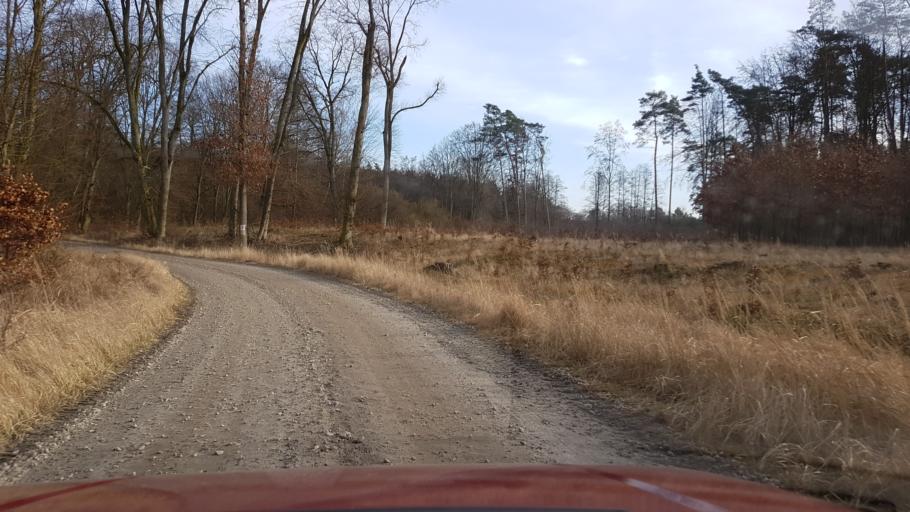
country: PL
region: West Pomeranian Voivodeship
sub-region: Powiat choszczenski
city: Pelczyce
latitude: 52.9123
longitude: 15.3756
